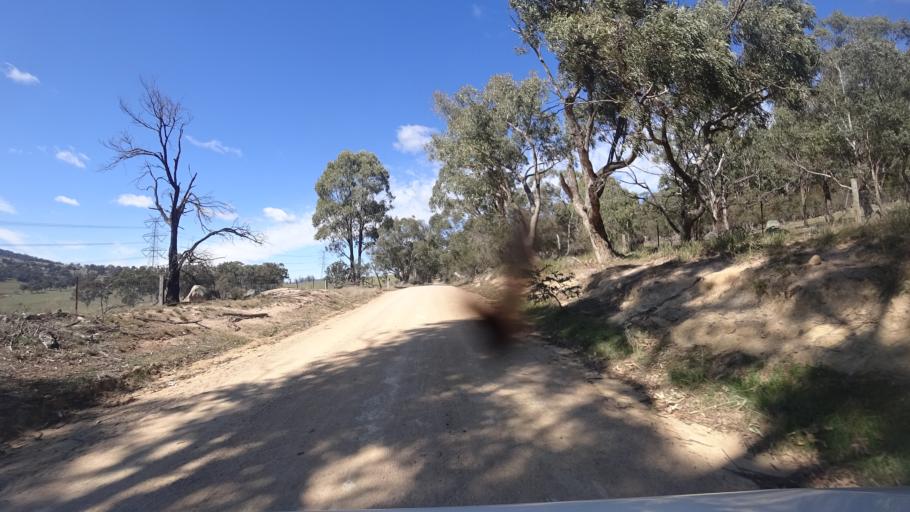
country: AU
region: New South Wales
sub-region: Lithgow
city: Portland
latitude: -33.5335
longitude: 149.9337
